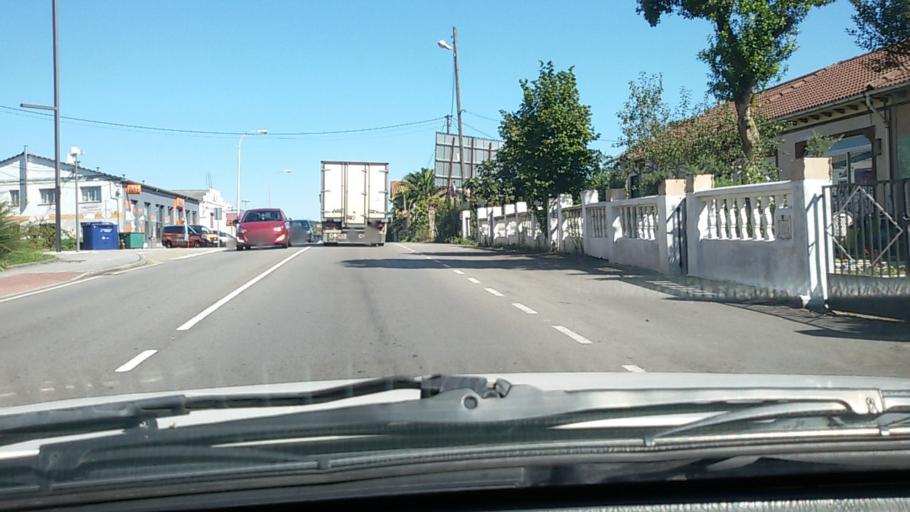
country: ES
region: Asturias
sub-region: Province of Asturias
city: Lugones
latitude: 43.4072
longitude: -5.8050
